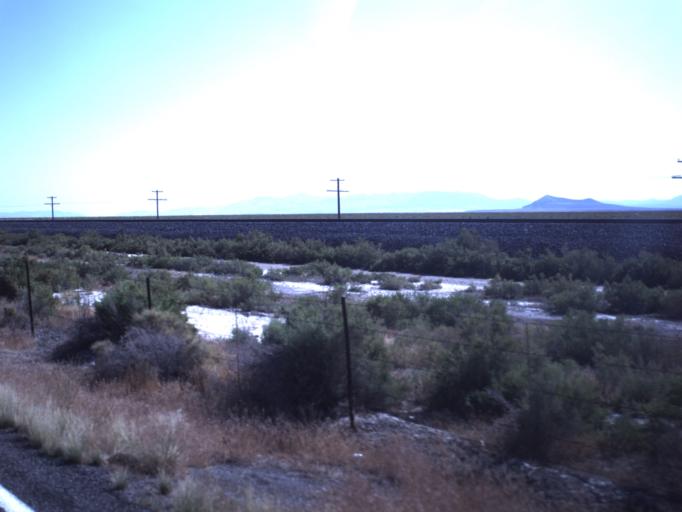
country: US
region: Utah
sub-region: Millard County
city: Delta
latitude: 39.0649
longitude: -112.7616
